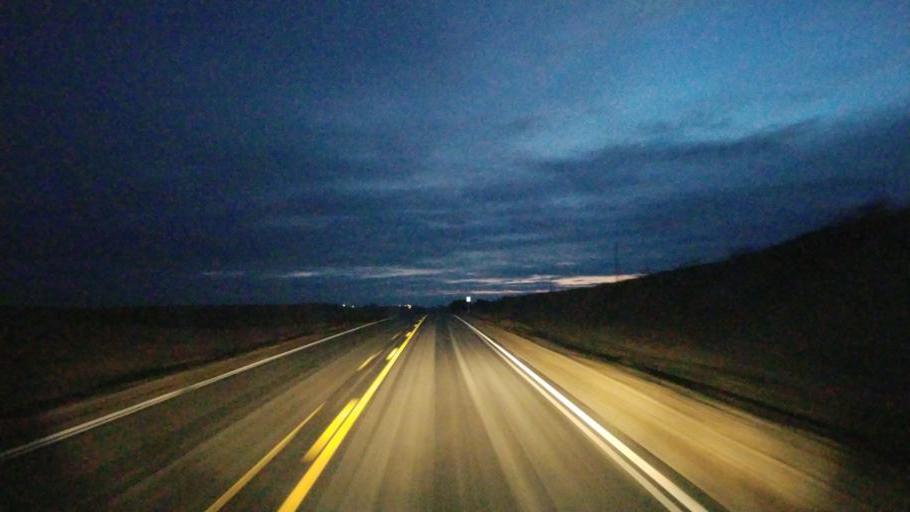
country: US
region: Nebraska
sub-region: Knox County
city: Center
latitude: 42.5971
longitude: -97.8269
